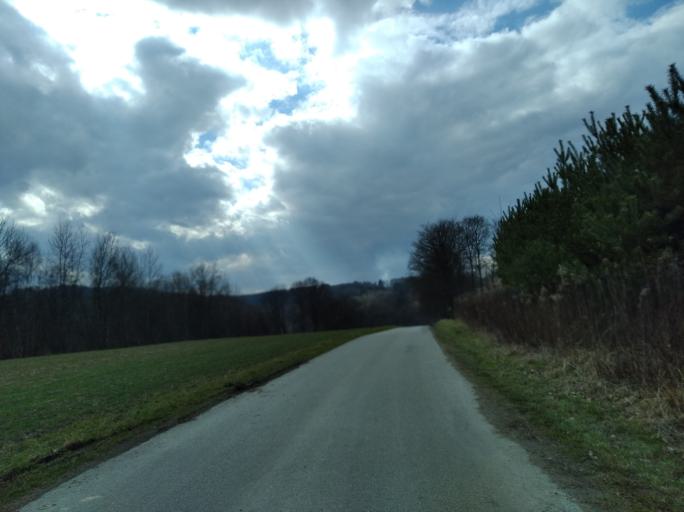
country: PL
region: Subcarpathian Voivodeship
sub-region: Powiat strzyzowski
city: Wysoka Strzyzowska
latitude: 49.7939
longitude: 21.7277
